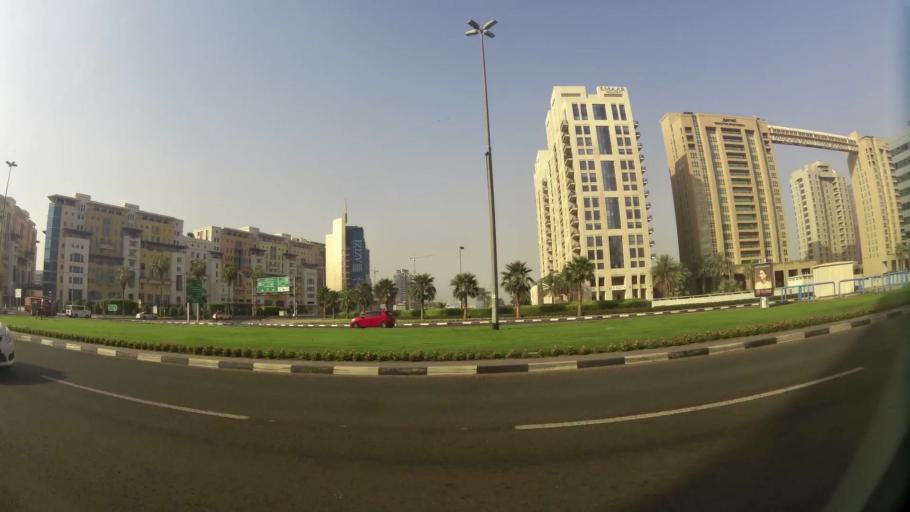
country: AE
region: Ash Shariqah
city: Sharjah
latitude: 25.2592
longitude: 55.3257
